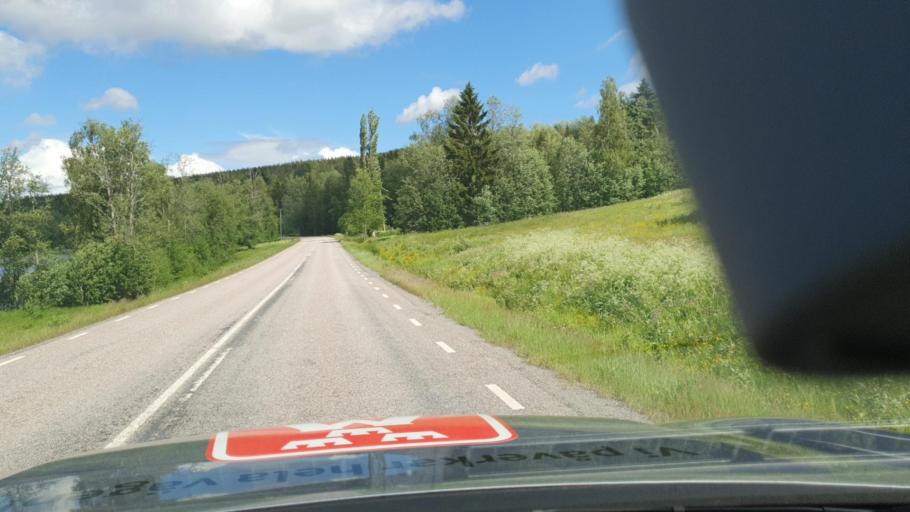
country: SE
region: Vaesternorrland
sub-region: OErnskoeldsviks Kommun
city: Bjasta
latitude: 63.2805
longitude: 18.2934
